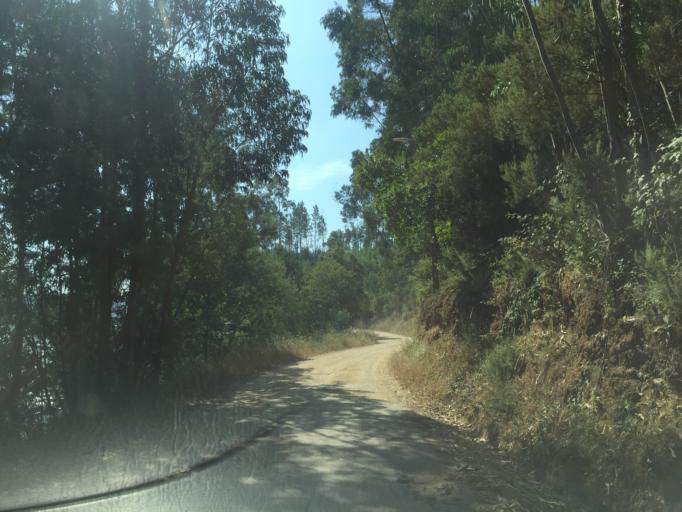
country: PT
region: Santarem
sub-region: Ferreira do Zezere
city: Ferreira do Zezere
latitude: 39.6080
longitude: -8.2788
